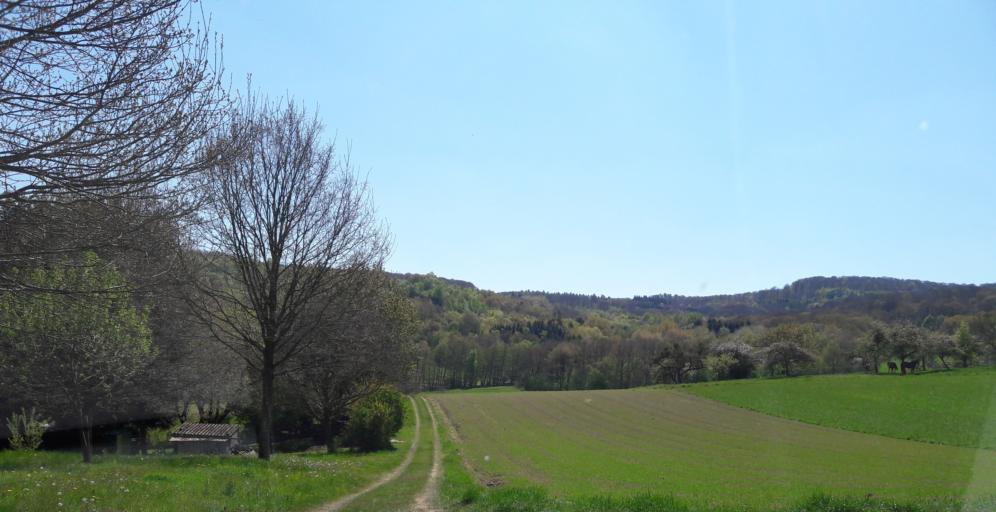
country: DE
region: Rheinland-Pfalz
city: Pfeffelbach
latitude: 49.5364
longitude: 7.3222
